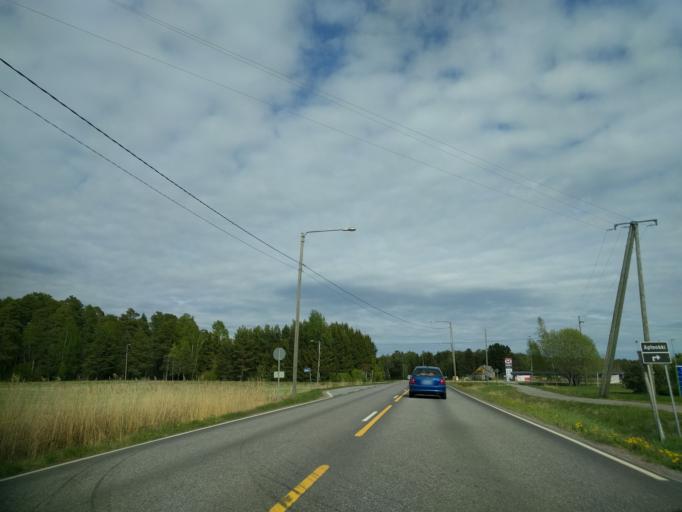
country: FI
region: Varsinais-Suomi
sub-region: Vakka-Suomi
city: Taivassalo
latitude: 60.5647
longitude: 21.6125
